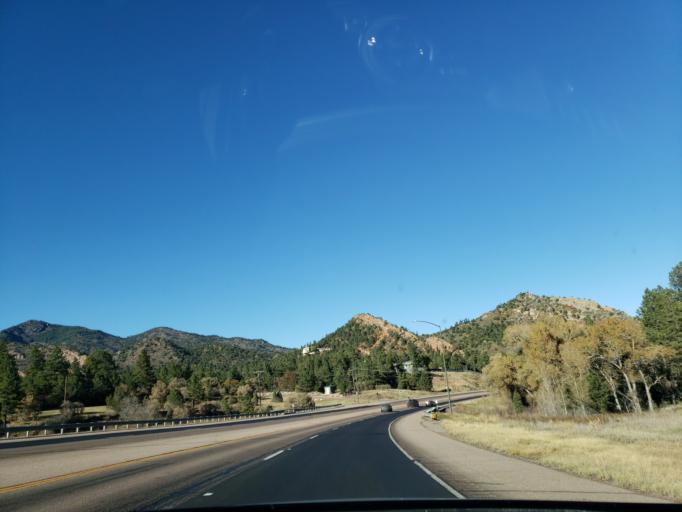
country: US
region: Colorado
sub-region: El Paso County
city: Fort Carson
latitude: 38.6678
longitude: -104.8628
